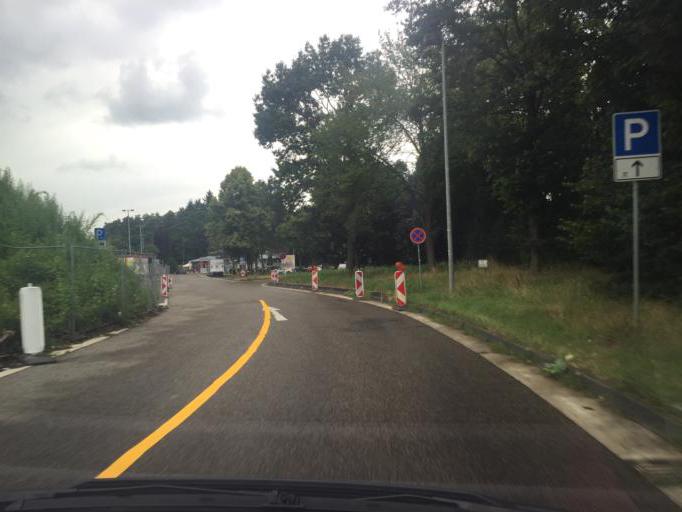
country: DE
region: North Rhine-Westphalia
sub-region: Regierungsbezirk Koln
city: Rosrath
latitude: 50.8988
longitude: 7.1535
